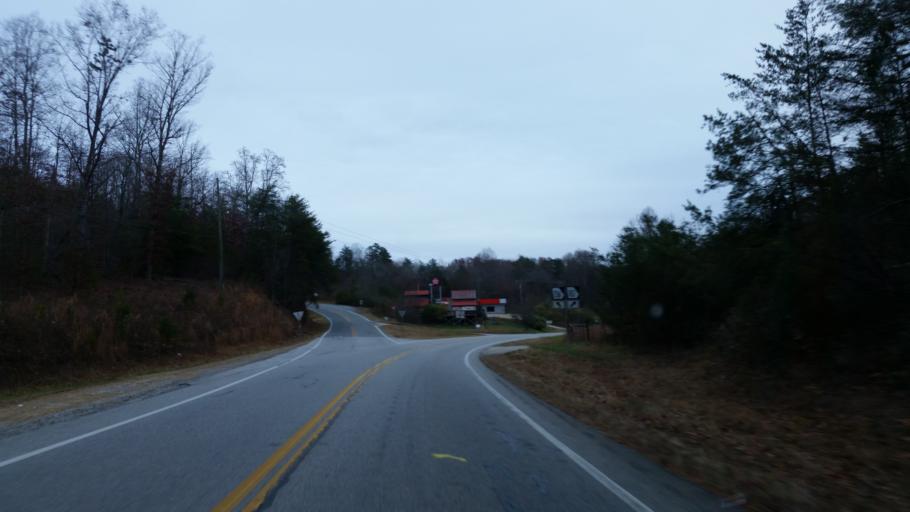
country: US
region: Georgia
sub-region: Dawson County
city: Dawsonville
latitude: 34.5124
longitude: -84.2293
